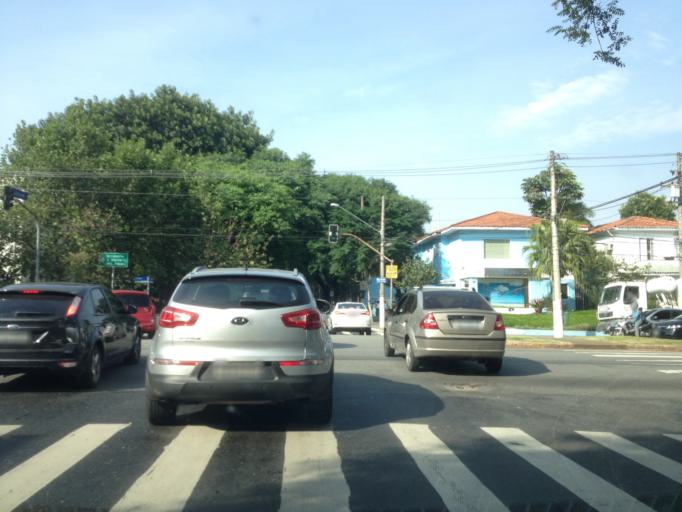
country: BR
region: Sao Paulo
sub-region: Sao Paulo
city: Sao Paulo
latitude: -23.5754
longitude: -46.6653
